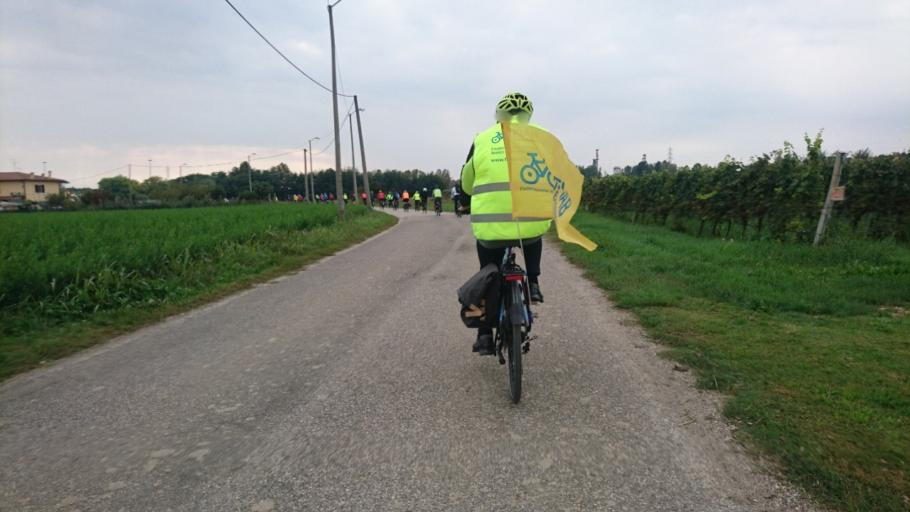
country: IT
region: Veneto
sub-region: Provincia di Verona
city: San Giovanni Lupatoto
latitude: 45.4074
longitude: 11.0591
